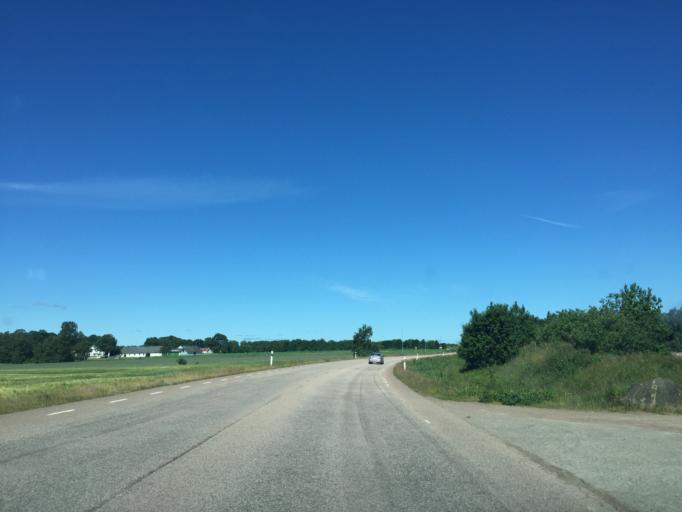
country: SE
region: Skane
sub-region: Angelholms Kommun
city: AEngelholm
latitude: 56.2235
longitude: 12.8445
